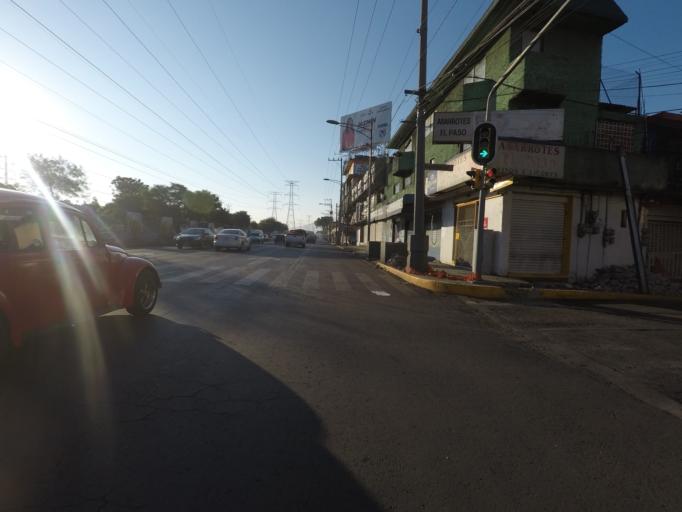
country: MX
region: Mexico City
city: Iztapalapa
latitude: 19.3695
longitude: -99.0770
